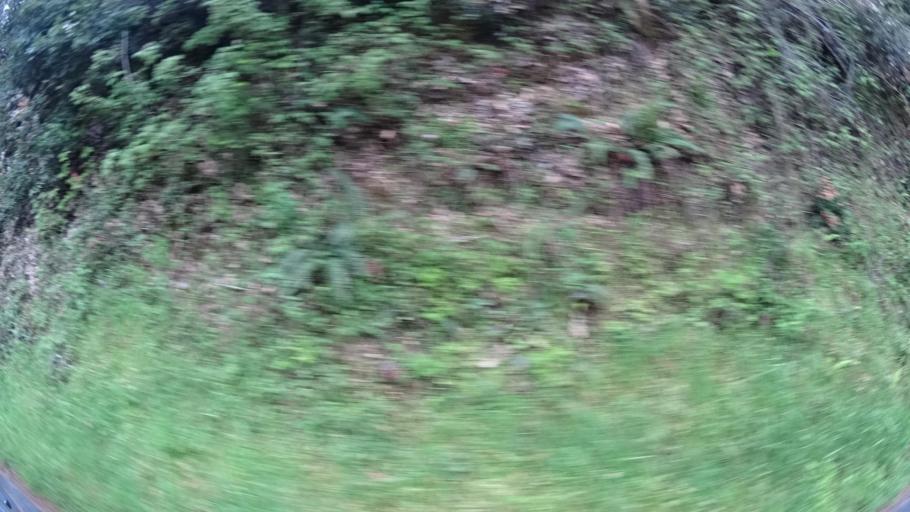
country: US
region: California
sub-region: Humboldt County
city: Redway
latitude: 40.2776
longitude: -123.7906
